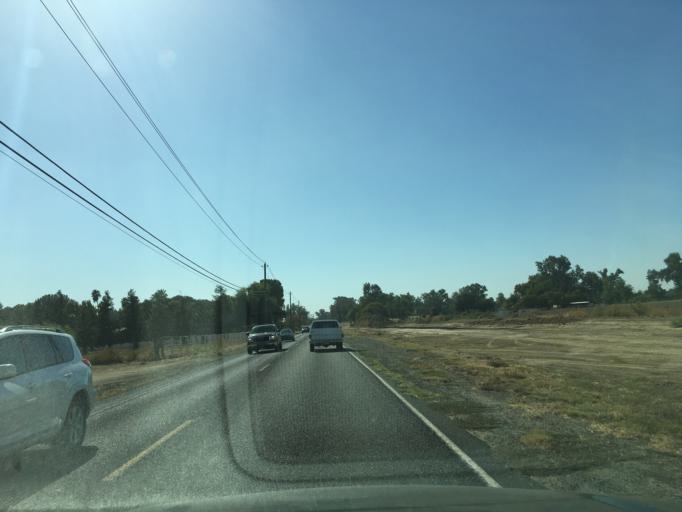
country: US
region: California
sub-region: Madera County
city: Parksdale
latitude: 36.9923
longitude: -120.0067
